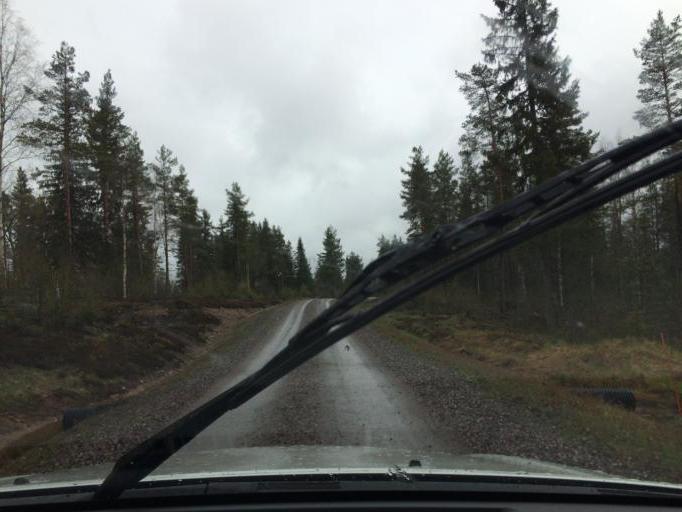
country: SE
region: OErebro
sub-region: Hallefors Kommun
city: Haellefors
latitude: 60.0366
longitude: 14.5315
